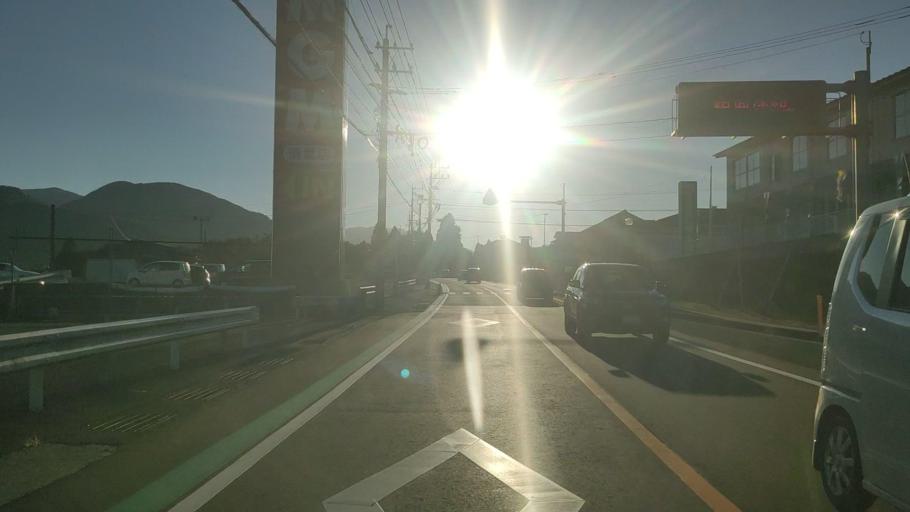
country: JP
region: Miyazaki
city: Miyazaki-shi
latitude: 31.8428
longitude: 131.3411
